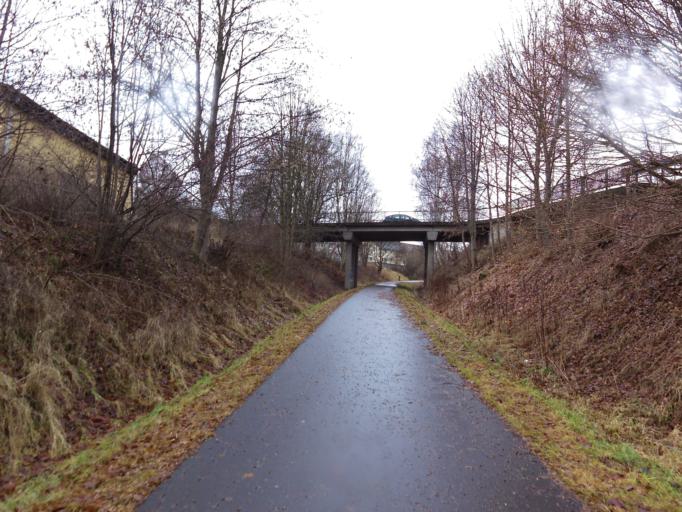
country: DE
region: Bavaria
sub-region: Upper Franconia
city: Wunsiedel
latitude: 50.0421
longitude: 12.0100
